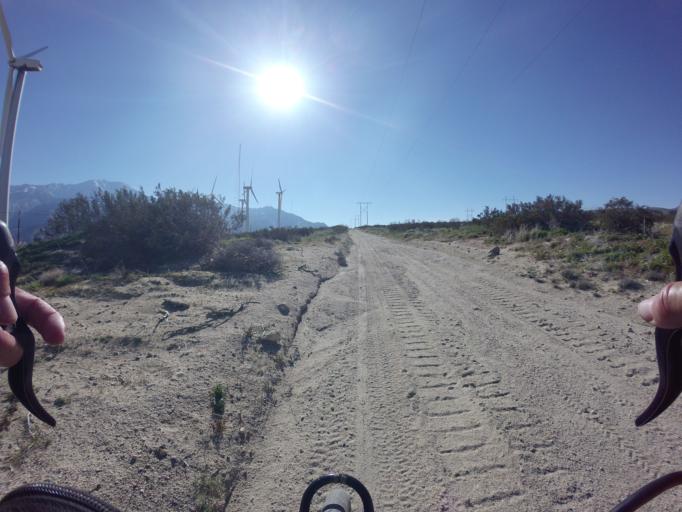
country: US
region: California
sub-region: Riverside County
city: Garnet
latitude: 33.9306
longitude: -116.6283
